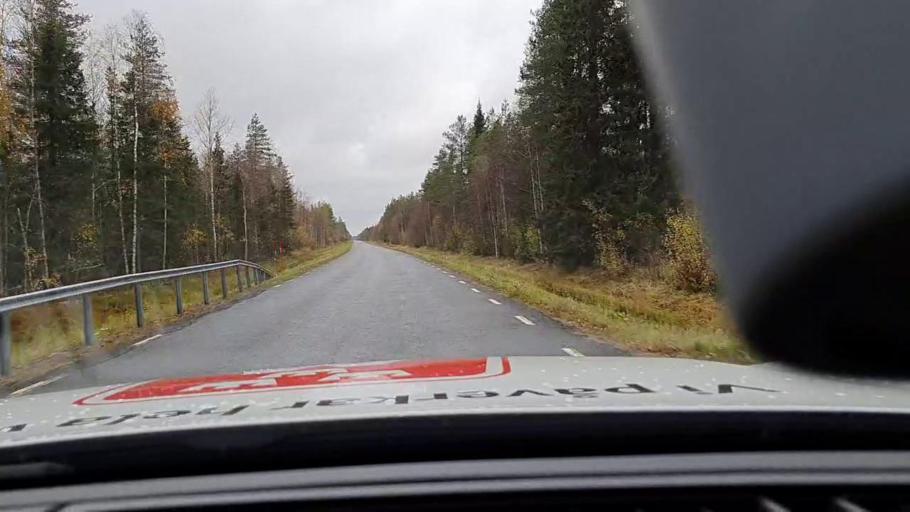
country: SE
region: Norrbotten
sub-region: Haparanda Kommun
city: Haparanda
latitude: 65.9047
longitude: 23.8333
